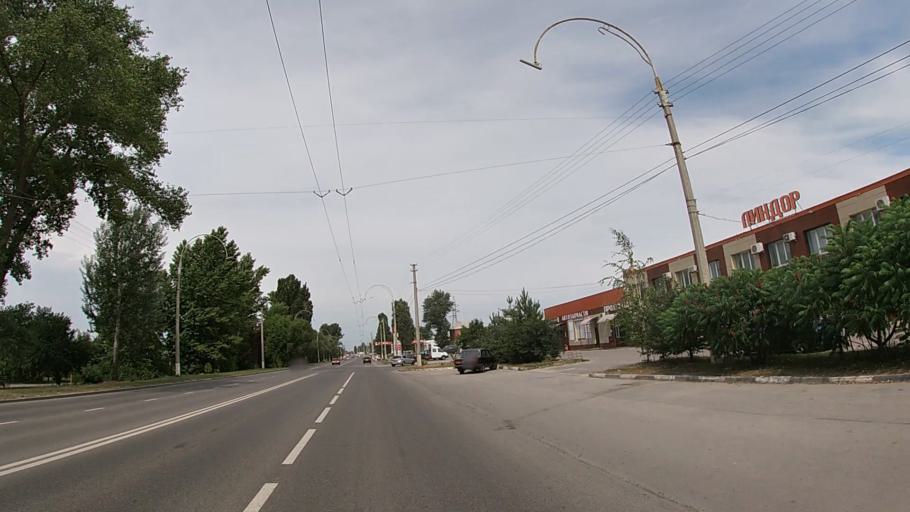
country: RU
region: Belgorod
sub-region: Belgorodskiy Rayon
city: Belgorod
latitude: 50.6099
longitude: 36.5444
